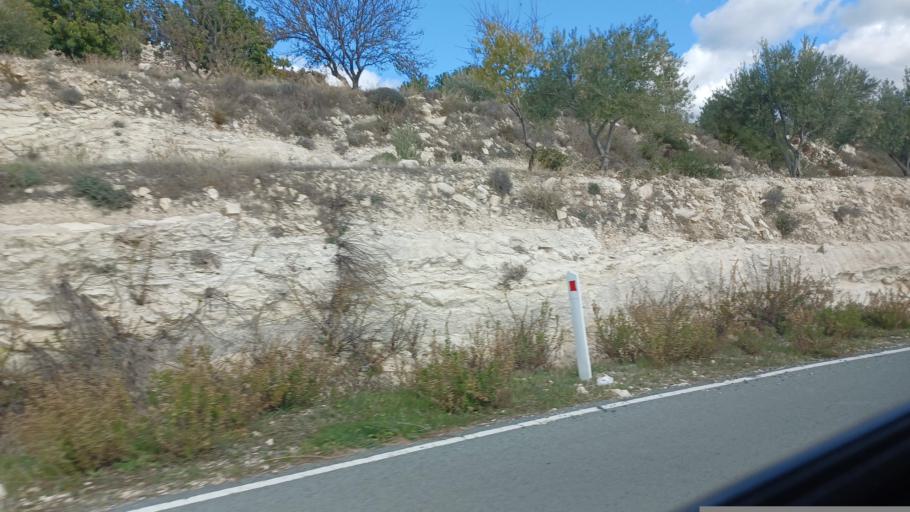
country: CY
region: Limassol
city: Pano Polemidia
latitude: 34.7932
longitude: 32.9875
